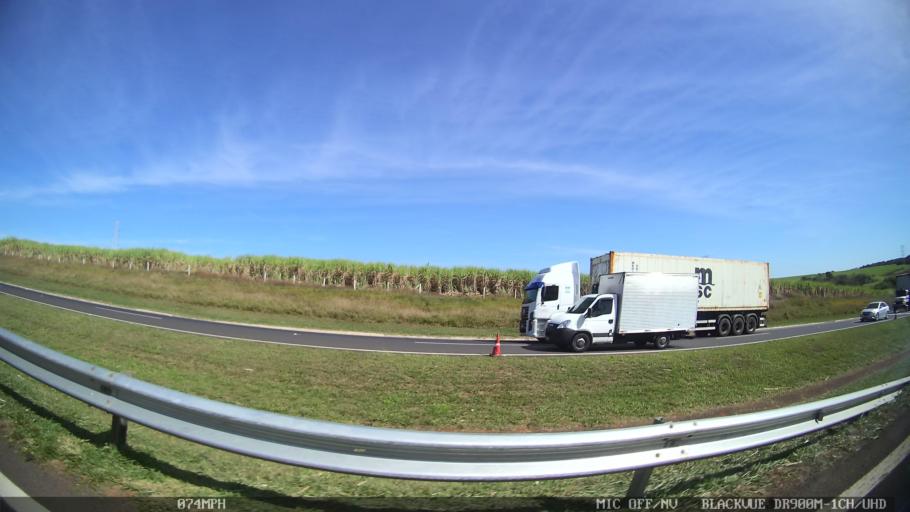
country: BR
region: Sao Paulo
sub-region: Porto Ferreira
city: Porto Ferreira
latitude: -21.9189
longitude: -47.4728
